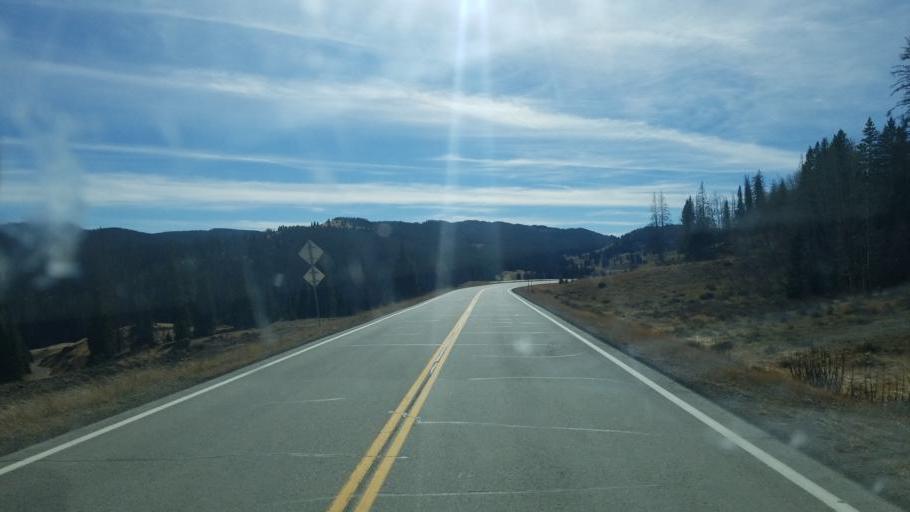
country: US
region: New Mexico
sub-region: Rio Arriba County
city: Chama
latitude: 37.0168
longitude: -106.4178
